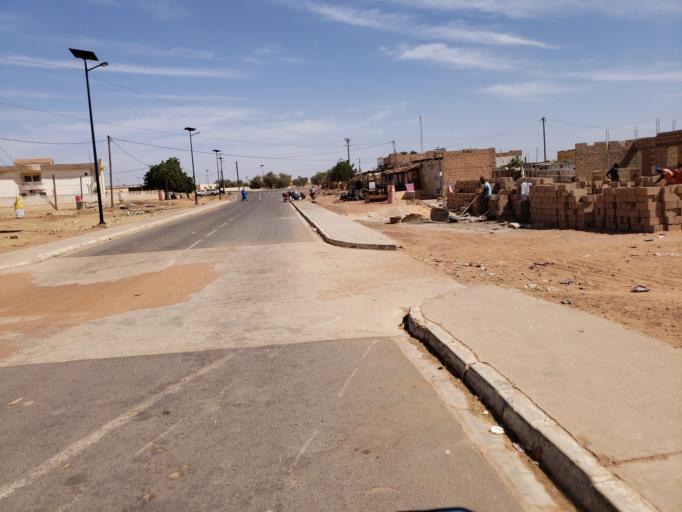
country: SN
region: Matam
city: Ranerou
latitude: 15.2986
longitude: -13.9581
